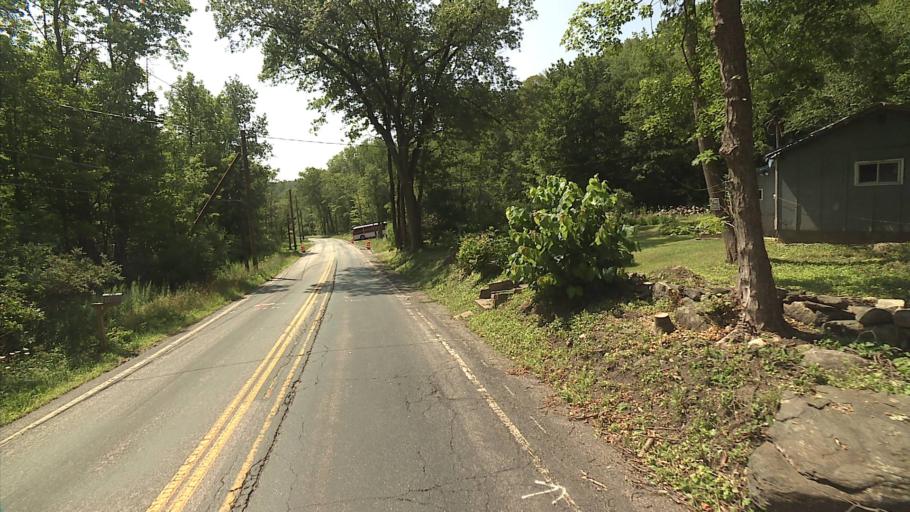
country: US
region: Connecticut
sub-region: Litchfield County
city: Winchester Center
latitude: 41.9241
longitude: -73.2082
